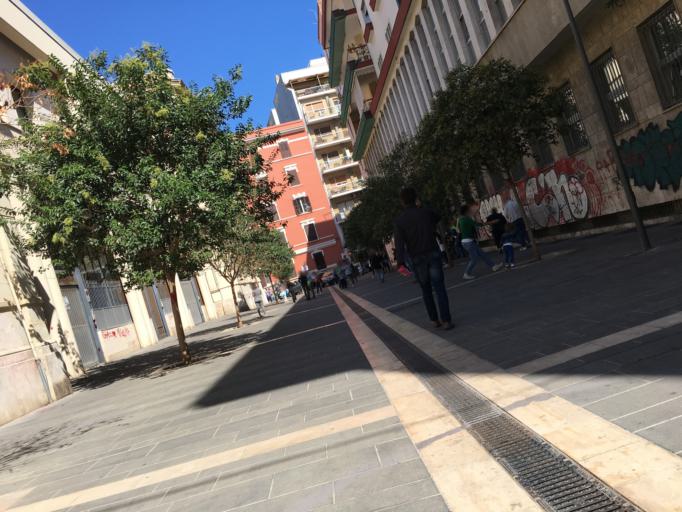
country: IT
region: Apulia
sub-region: Provincia di Bari
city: Bari
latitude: 41.1195
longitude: 16.8800
